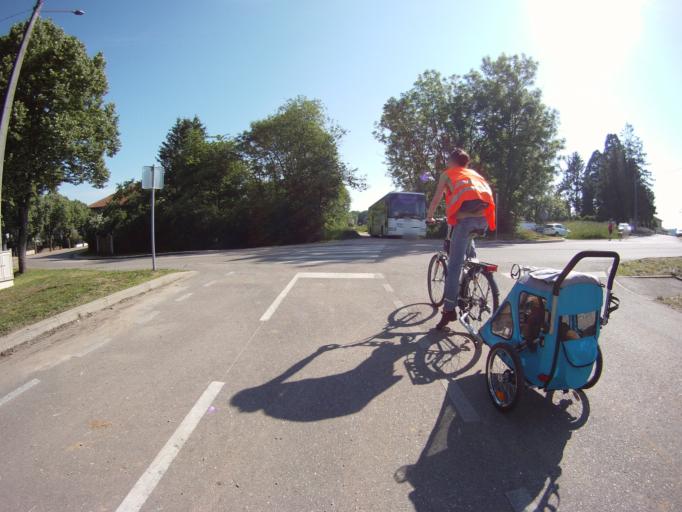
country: FR
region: Lorraine
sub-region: Departement de Meurthe-et-Moselle
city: Champenoux
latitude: 48.7730
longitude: 6.3615
